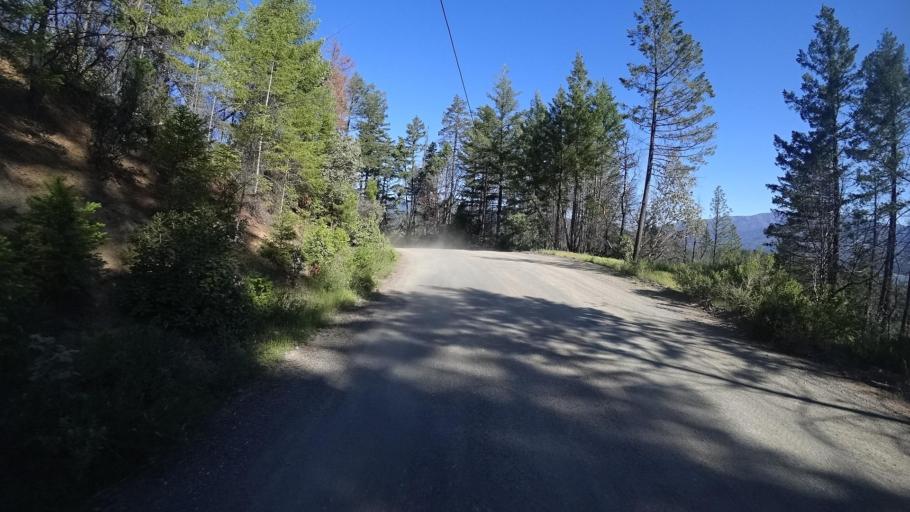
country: US
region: California
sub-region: Lake County
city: Upper Lake
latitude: 39.4029
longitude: -122.9630
